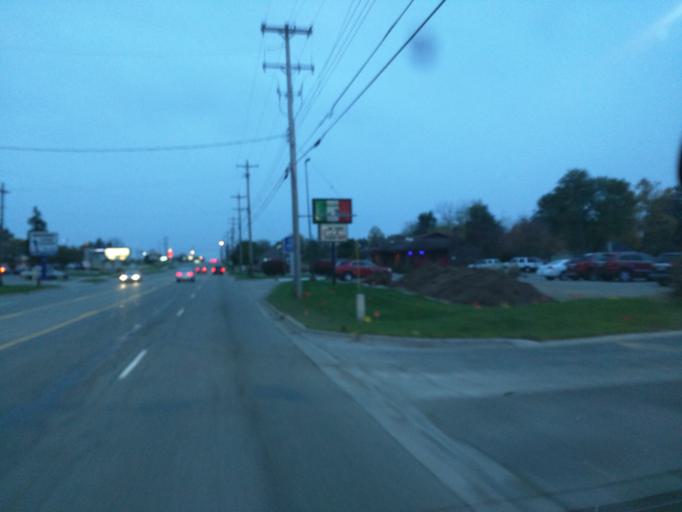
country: US
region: Michigan
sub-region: Ingham County
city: Edgemont Park
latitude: 42.7327
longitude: -84.6031
